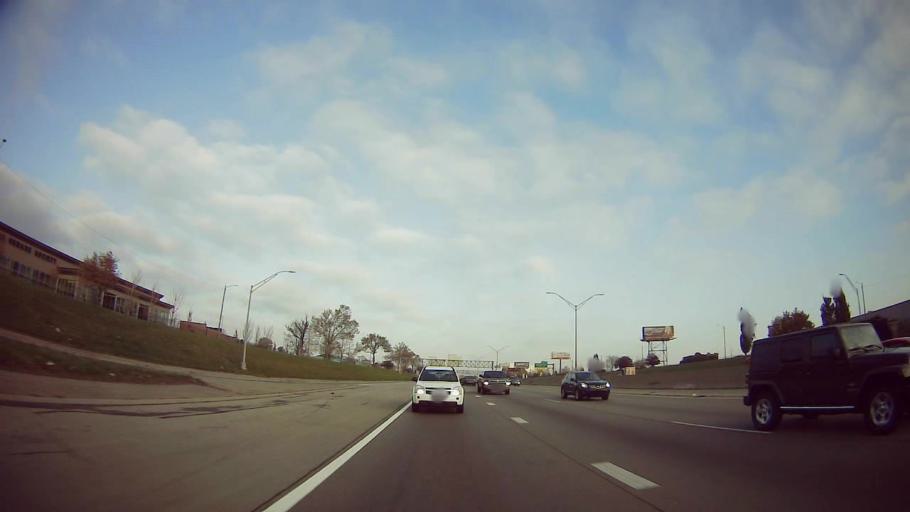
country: US
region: Michigan
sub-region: Wayne County
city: Hamtramck
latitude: 42.3800
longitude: -83.0641
